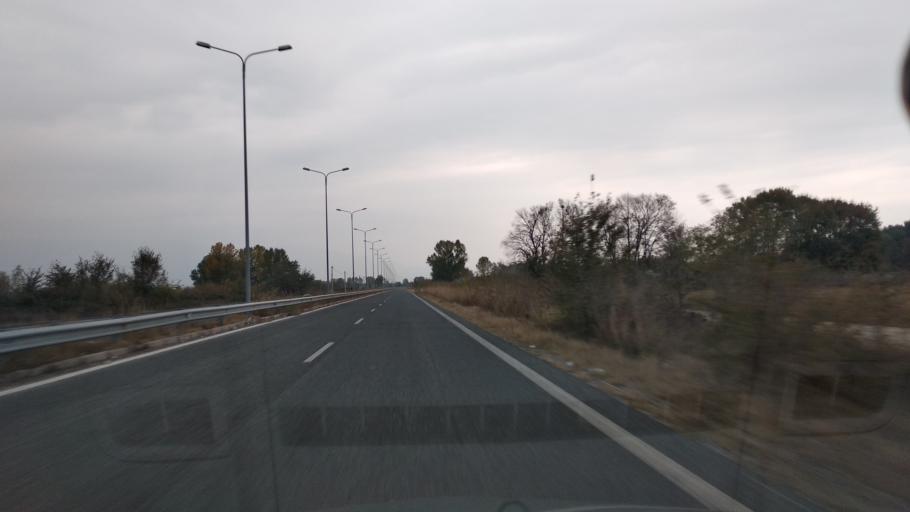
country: GR
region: Thessaly
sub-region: Trikala
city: Pyrgetos
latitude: 39.5316
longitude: 21.7424
